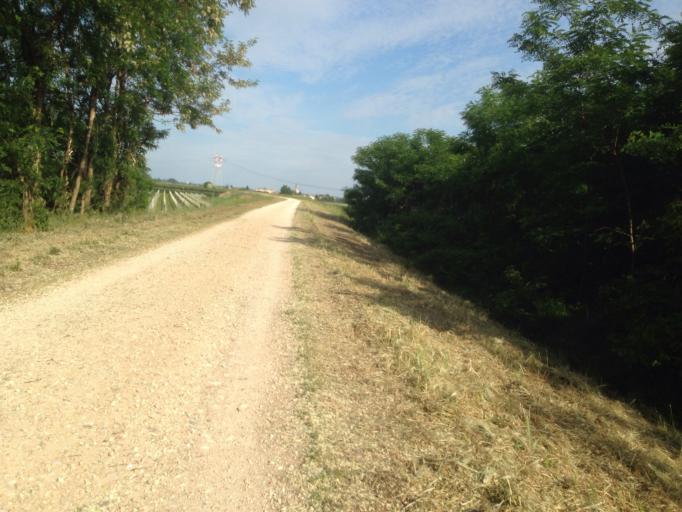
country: IT
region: Veneto
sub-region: Provincia di Verona
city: Zevio
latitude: 45.3698
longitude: 11.1709
